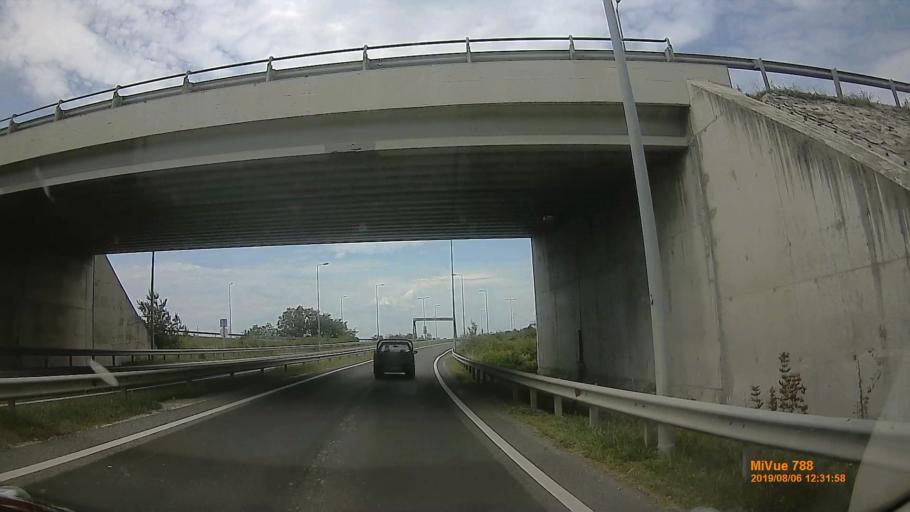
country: HU
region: Vas
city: Szombathely
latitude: 47.2479
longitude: 16.6549
